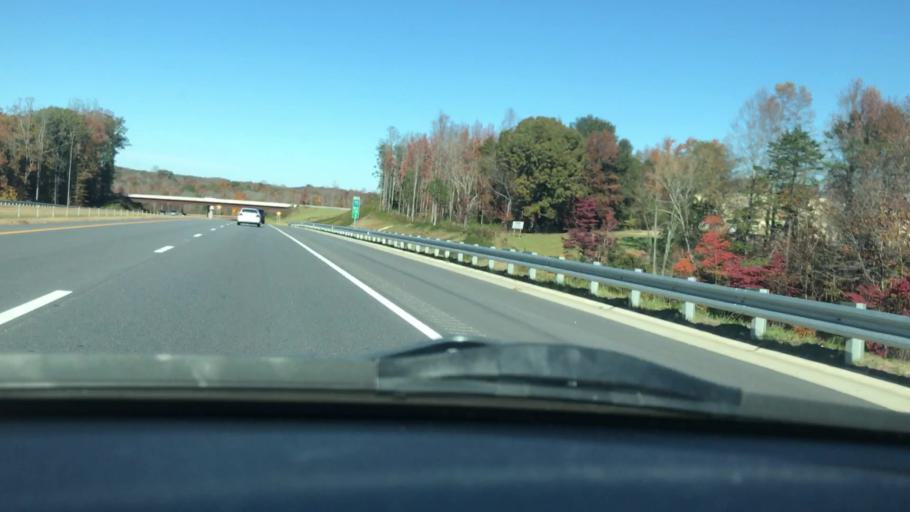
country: US
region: North Carolina
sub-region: Guilford County
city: Summerfield
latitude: 36.2219
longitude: -79.9142
